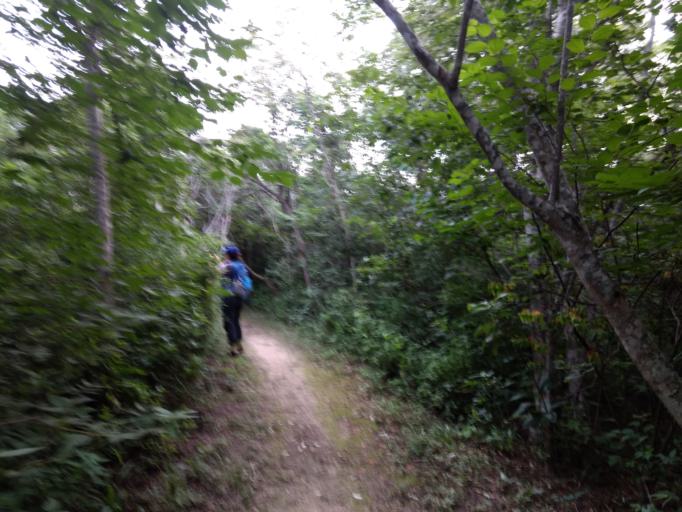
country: BR
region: Ceara
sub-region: Crateus
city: Crateus
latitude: -5.1427
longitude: -40.9212
